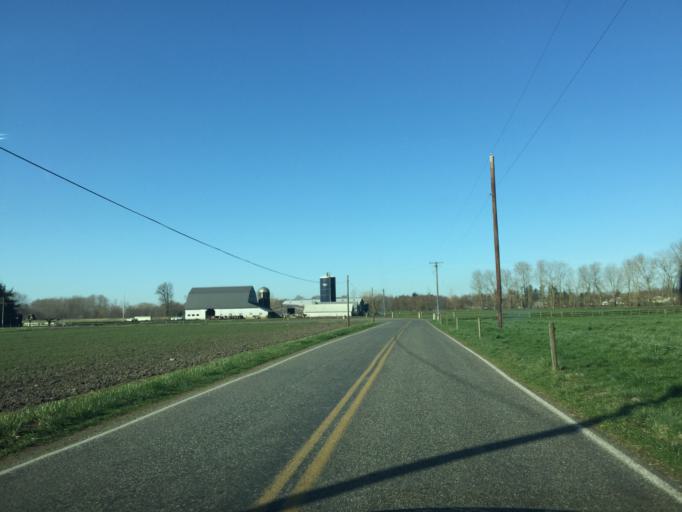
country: US
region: Washington
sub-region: Whatcom County
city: Lynden
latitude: 48.9351
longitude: -122.4507
